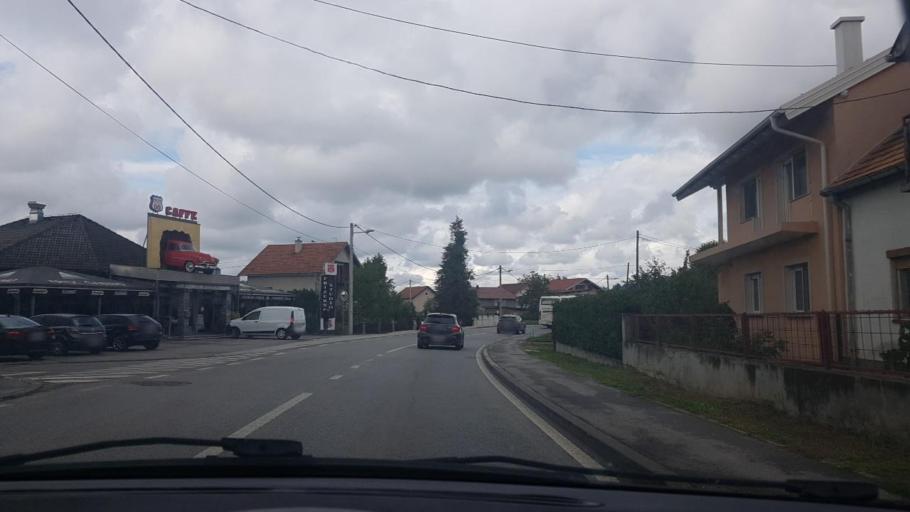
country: HR
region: Zagrebacka
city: Brdovec
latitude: 45.8695
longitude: 15.7550
